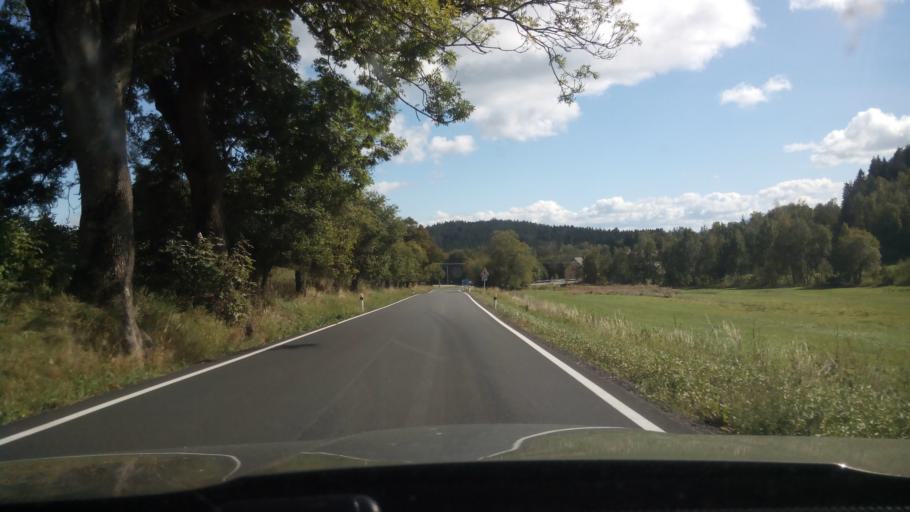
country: CZ
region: Jihocesky
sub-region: Okres Prachatice
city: Stachy
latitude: 49.1179
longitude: 13.6404
